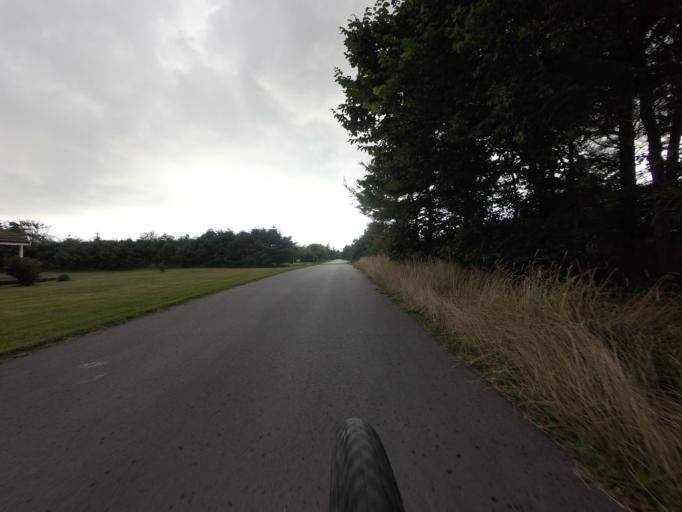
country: DK
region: North Denmark
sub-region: Hjorring Kommune
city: Hjorring
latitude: 57.4641
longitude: 9.8050
